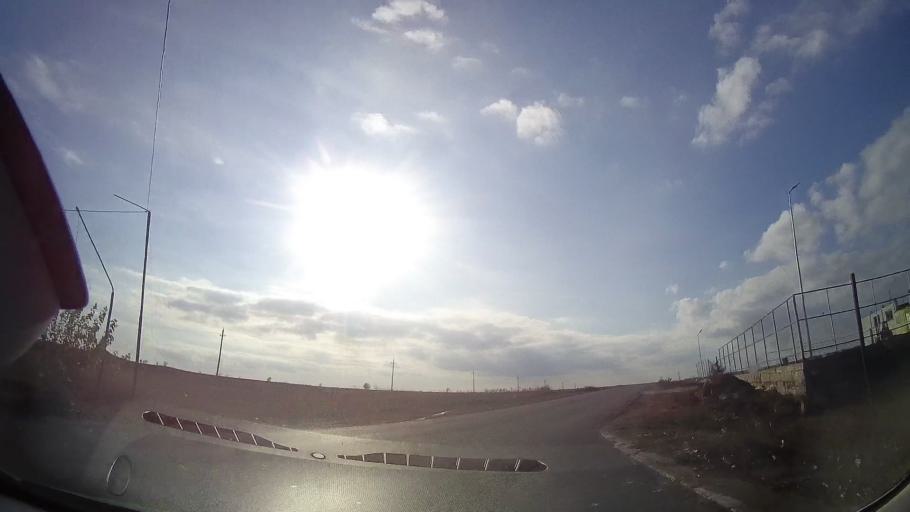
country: RO
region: Constanta
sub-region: Municipiul Mangalia
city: Mangalia
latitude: 43.7929
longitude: 28.5615
